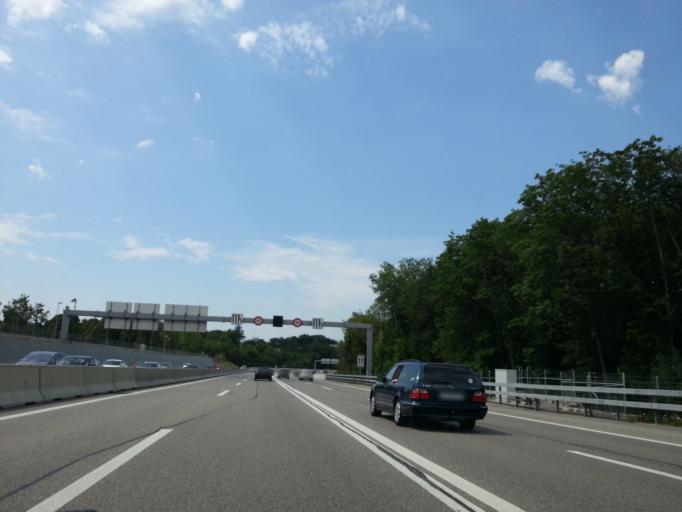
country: CH
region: Bern
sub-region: Bern-Mittelland District
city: Bern
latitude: 46.9697
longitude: 7.4635
